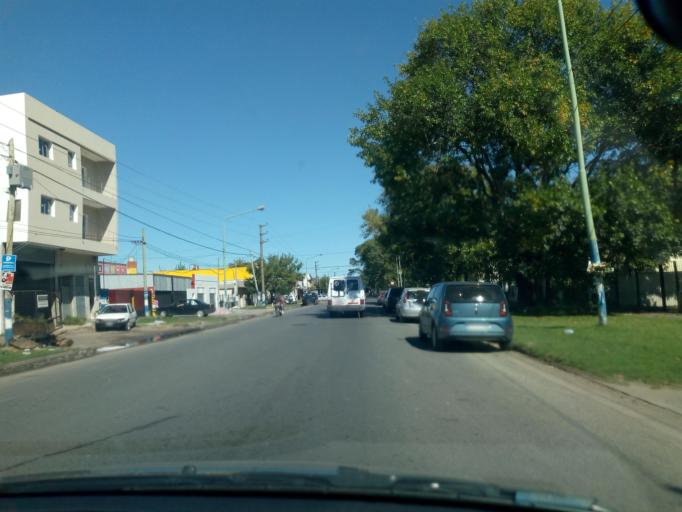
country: AR
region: Buenos Aires
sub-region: Partido de La Plata
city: La Plata
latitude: -34.9668
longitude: -57.9796
